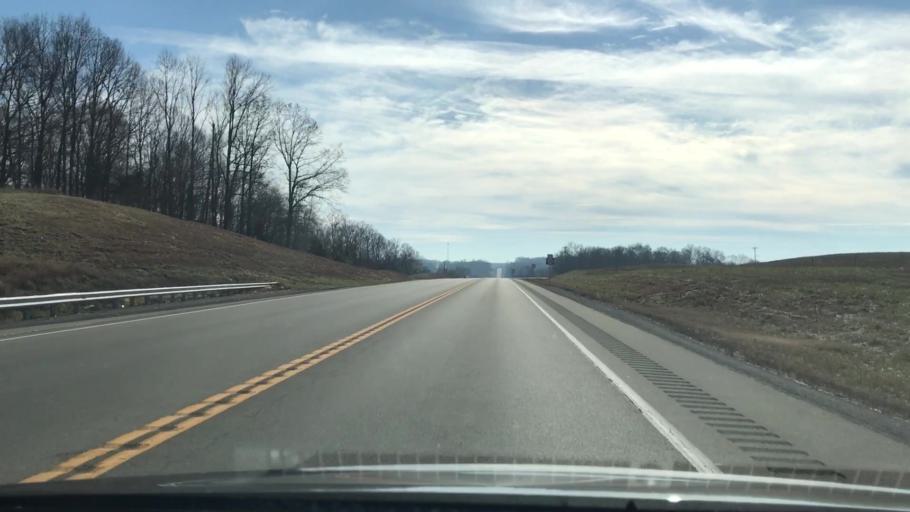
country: US
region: Kentucky
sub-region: Monroe County
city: Tompkinsville
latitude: 36.8172
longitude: -85.6884
